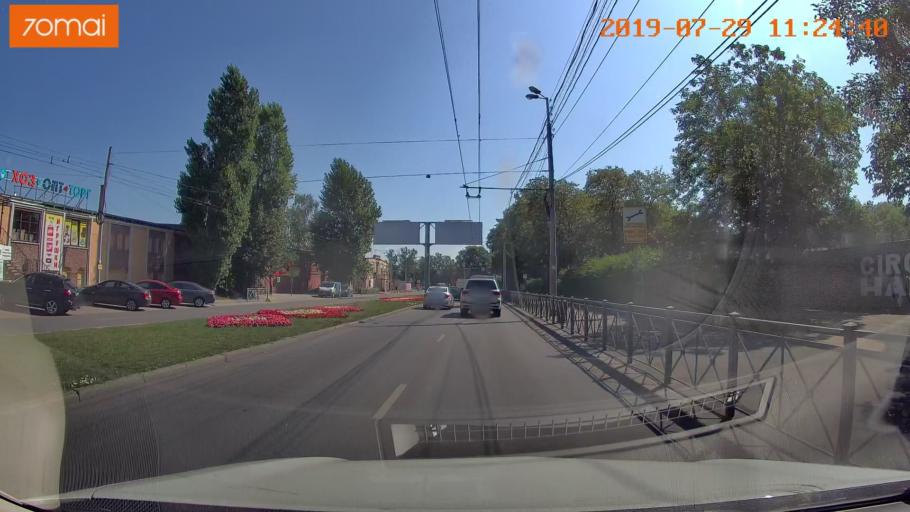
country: RU
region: Kaliningrad
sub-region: Gorod Kaliningrad
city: Kaliningrad
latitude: 54.6956
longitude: 20.5185
